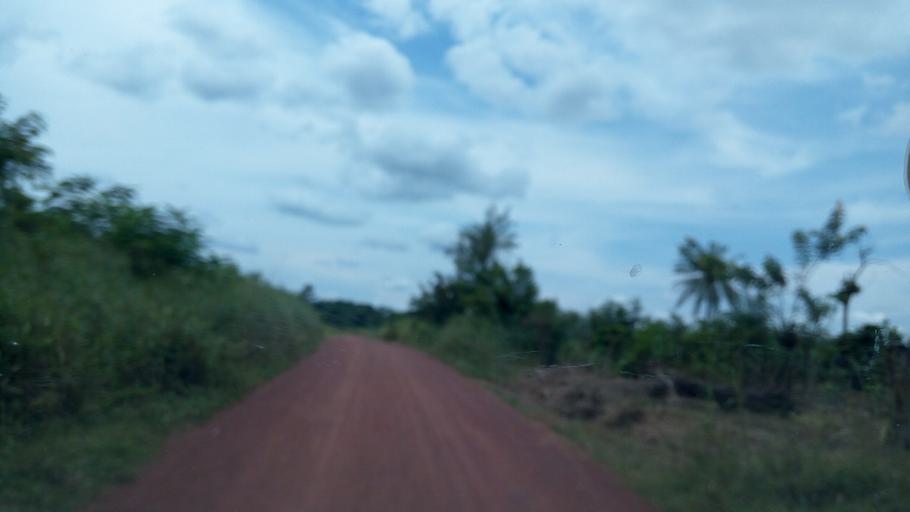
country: CD
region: Equateur
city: Libenge
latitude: 3.7477
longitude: 18.7886
